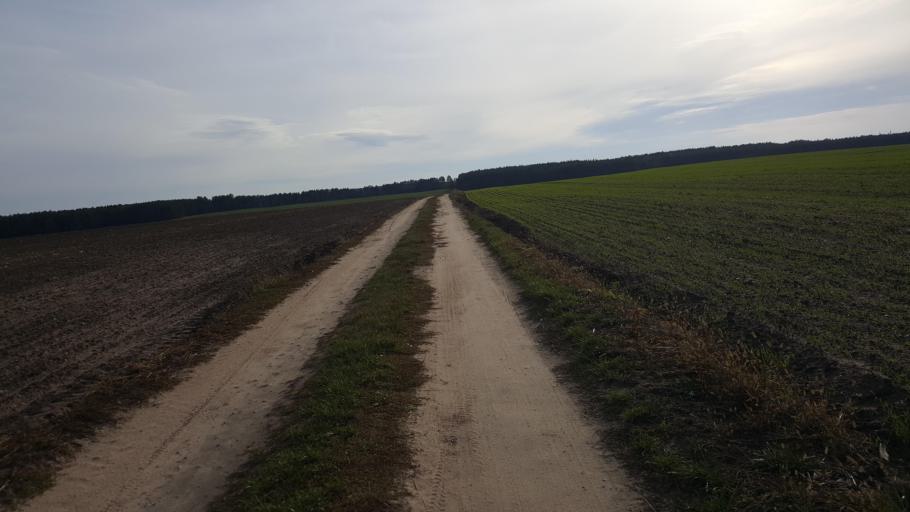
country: BY
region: Brest
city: Kamyanyets
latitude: 52.3962
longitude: 23.8538
